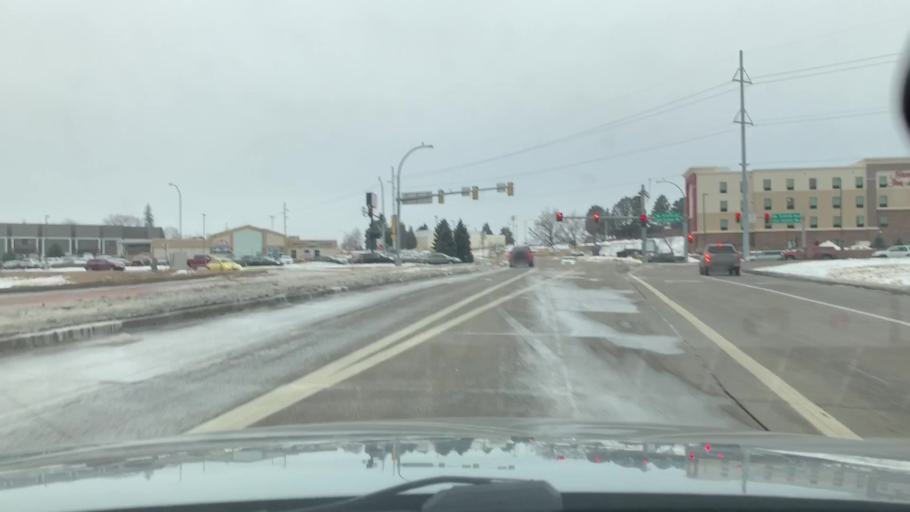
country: US
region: North Dakota
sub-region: Burleigh County
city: Bismarck
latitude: 46.8270
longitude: -100.8139
